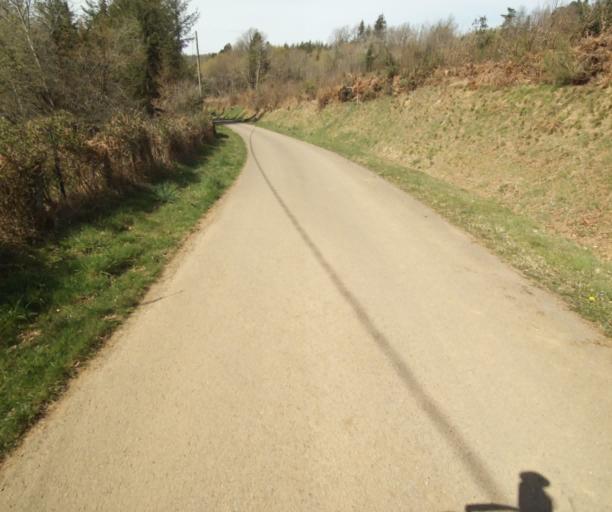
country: FR
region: Limousin
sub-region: Departement de la Correze
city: Seilhac
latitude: 45.3985
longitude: 1.7735
